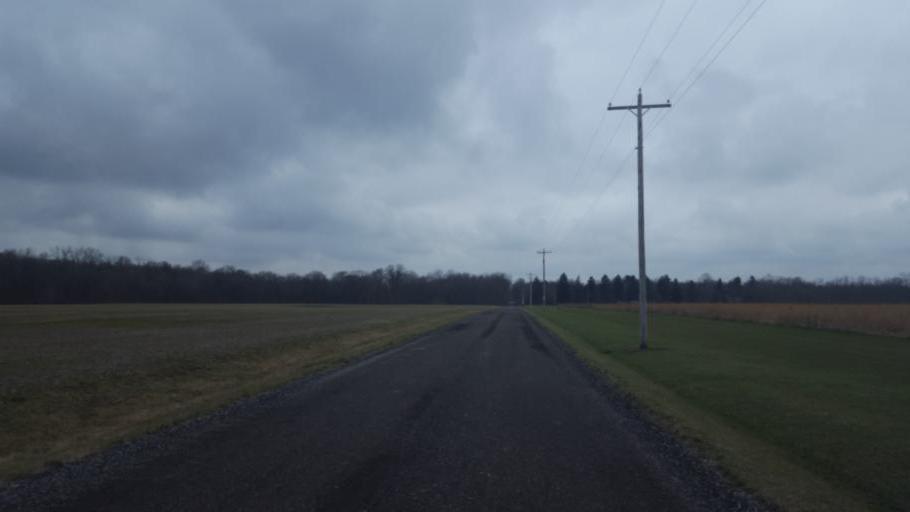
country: US
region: Ohio
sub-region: Delaware County
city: Ashley
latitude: 40.3734
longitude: -82.8690
